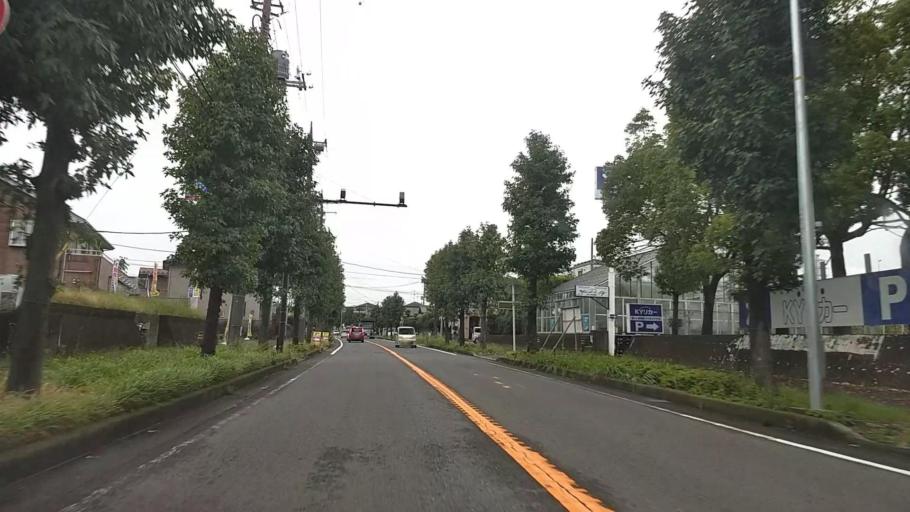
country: JP
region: Kanagawa
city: Fujisawa
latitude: 35.4136
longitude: 139.4741
